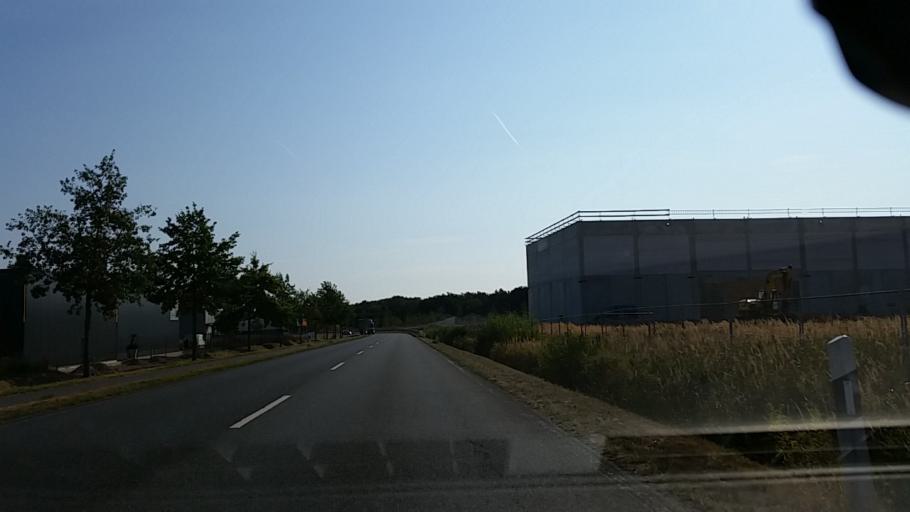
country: DE
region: Lower Saxony
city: Danndorf
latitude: 52.4239
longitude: 10.8674
